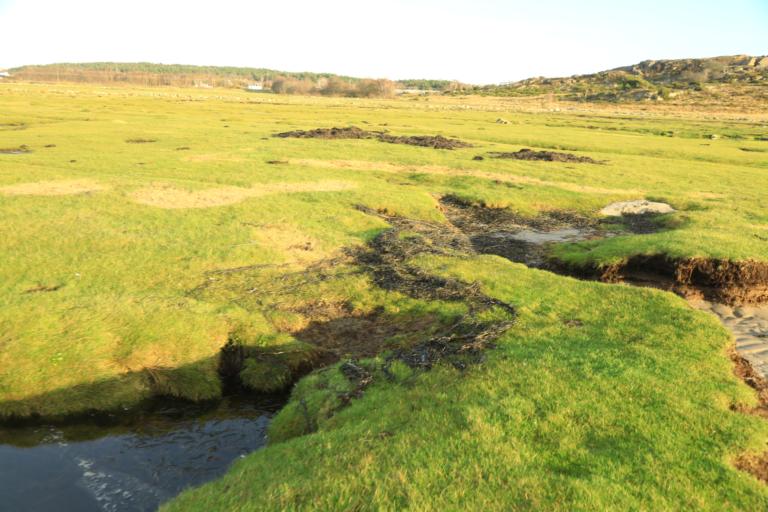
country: SE
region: Halland
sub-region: Varbergs Kommun
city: Varberg
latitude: 57.1623
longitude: 12.2274
